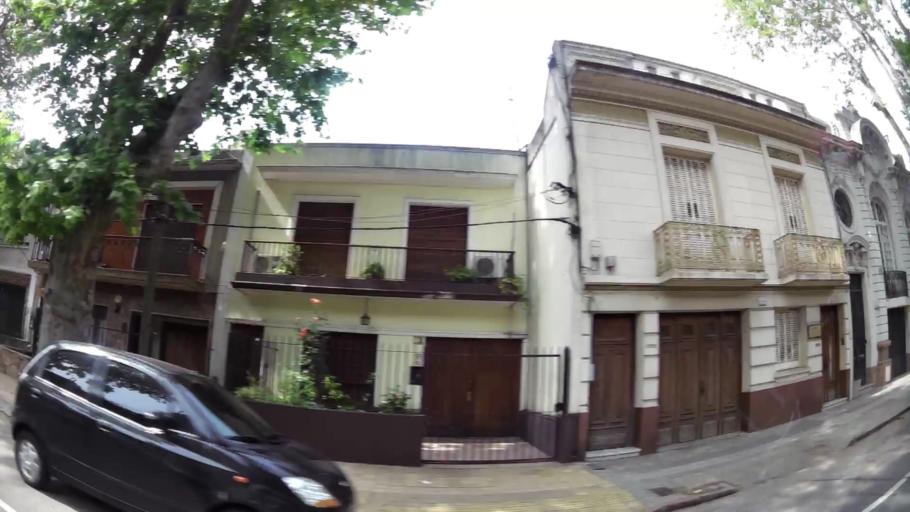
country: UY
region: Montevideo
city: Montevideo
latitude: -34.9079
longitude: -56.1654
